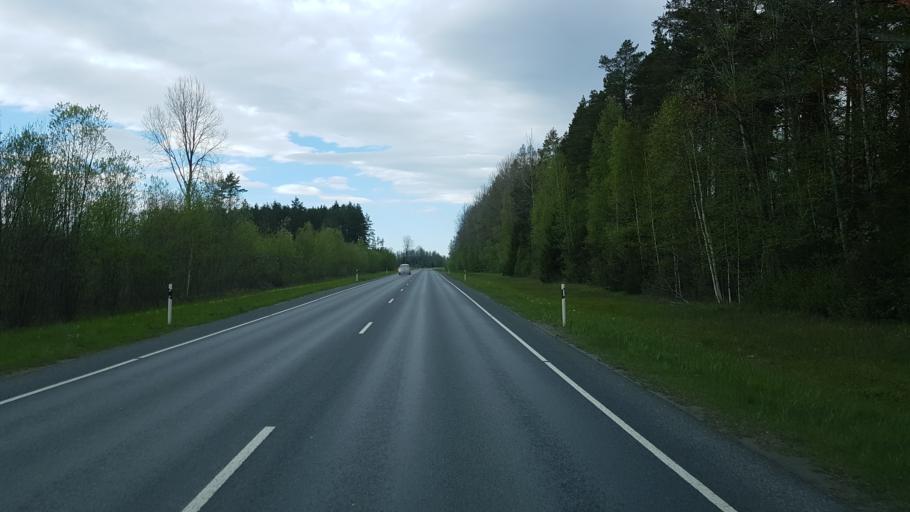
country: EE
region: Paernumaa
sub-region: Paikuse vald
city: Paikuse
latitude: 58.2156
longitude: 24.7118
